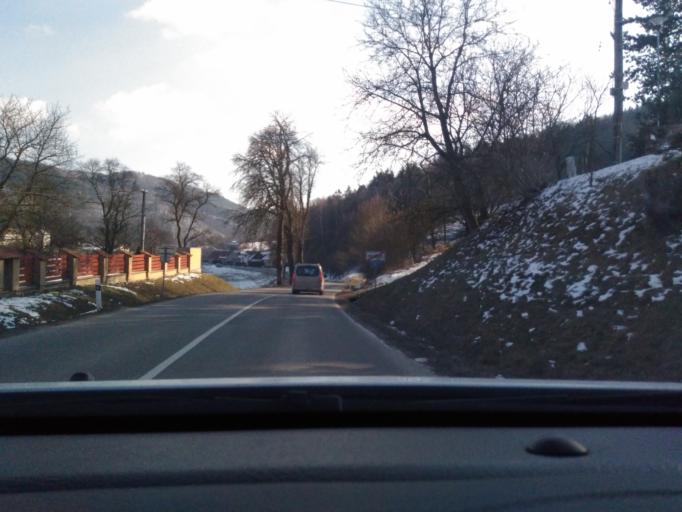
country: CZ
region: South Moravian
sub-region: Okres Brno-Venkov
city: Nedvedice
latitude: 49.4505
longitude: 16.3416
